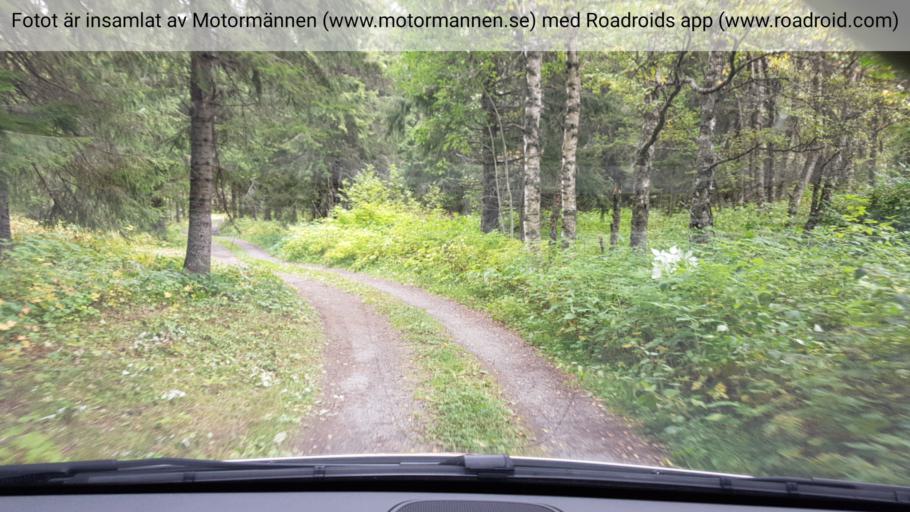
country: SE
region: Jaemtland
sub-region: OEstersunds Kommun
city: Ostersund
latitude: 63.1140
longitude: 14.6000
